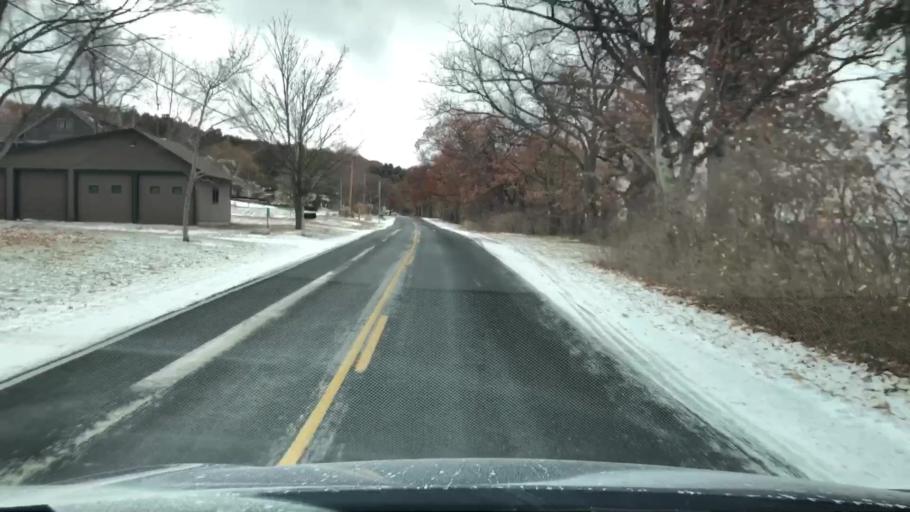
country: US
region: Michigan
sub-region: Grand Traverse County
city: Traverse City
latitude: 44.8070
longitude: -85.5812
